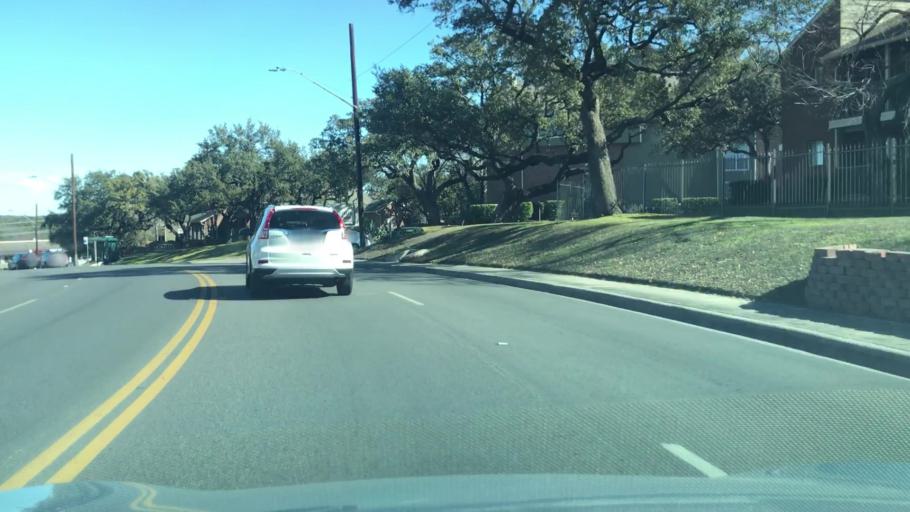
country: US
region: Texas
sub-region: Bexar County
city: Hollywood Park
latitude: 29.5915
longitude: -98.4705
